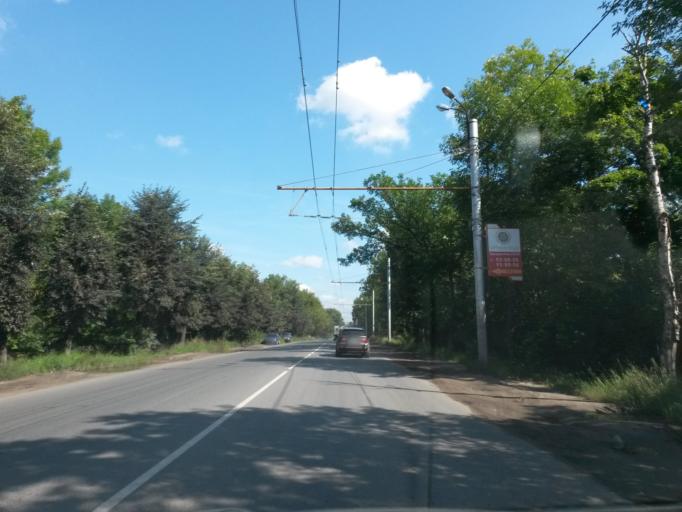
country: RU
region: Ivanovo
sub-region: Gorod Ivanovo
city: Ivanovo
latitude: 57.0039
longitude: 40.9461
